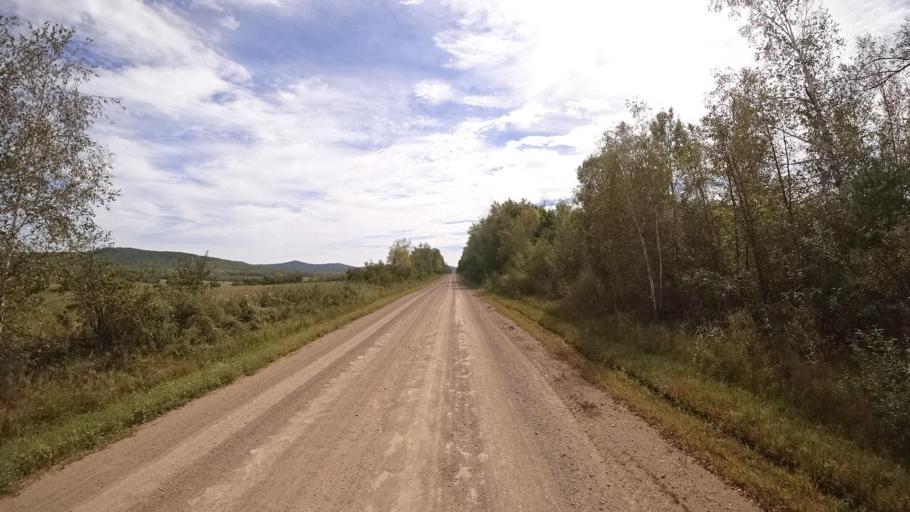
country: RU
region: Primorskiy
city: Yakovlevka
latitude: 44.6122
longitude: 133.5994
